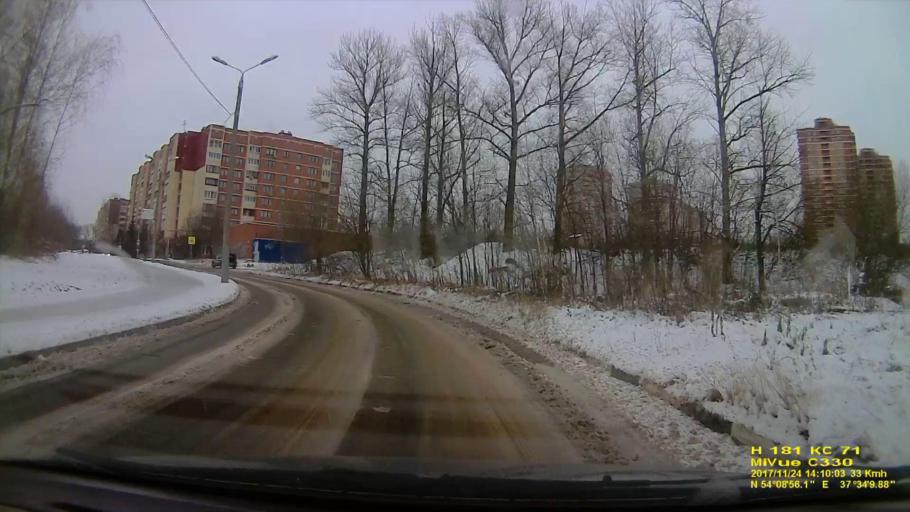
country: RU
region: Tula
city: Mendeleyevskiy
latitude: 54.1489
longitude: 37.5695
